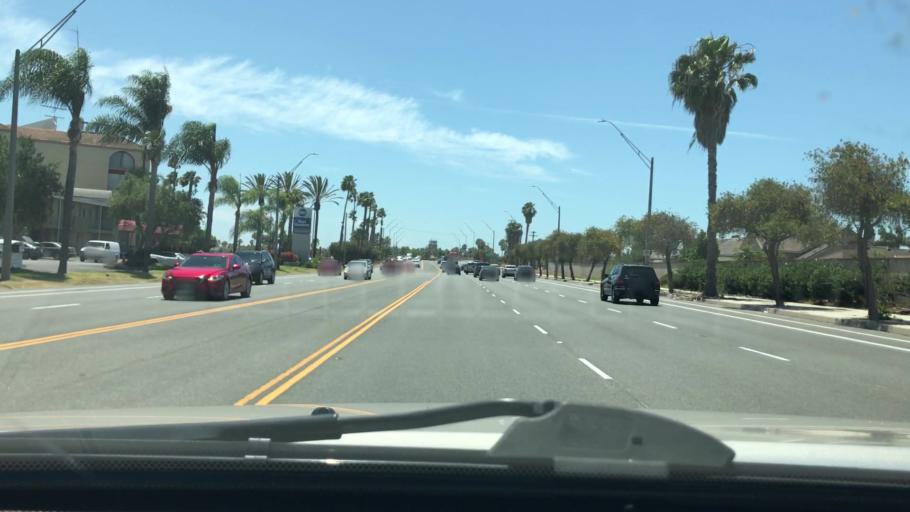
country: US
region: California
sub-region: Orange County
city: Seal Beach
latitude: 33.7661
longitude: -118.1165
